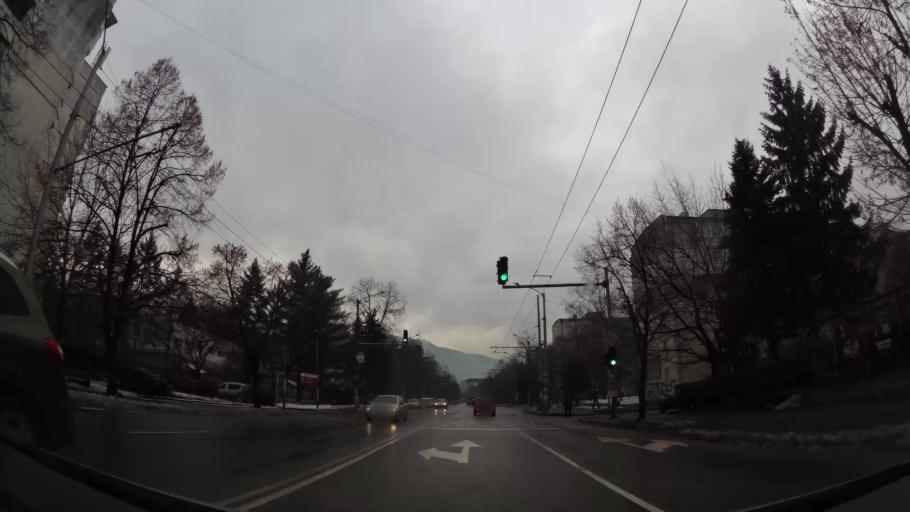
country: BG
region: Sofia-Capital
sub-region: Stolichna Obshtina
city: Sofia
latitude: 42.6714
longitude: 23.2832
